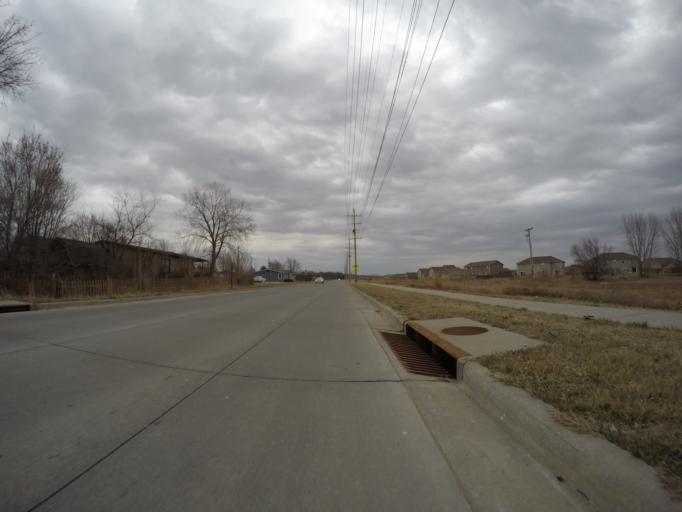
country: US
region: Kansas
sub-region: Riley County
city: Manhattan
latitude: 39.2187
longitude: -96.5663
